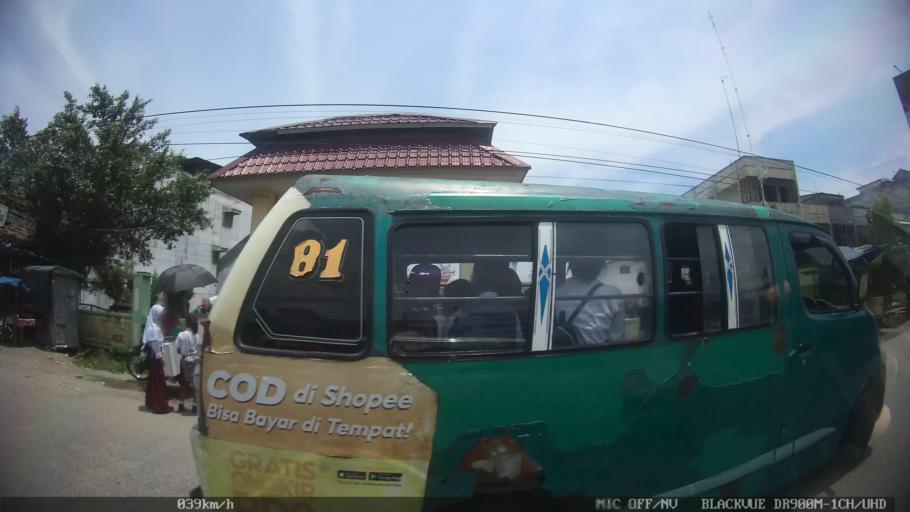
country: ID
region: North Sumatra
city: Labuhan Deli
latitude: 3.7225
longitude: 98.6801
